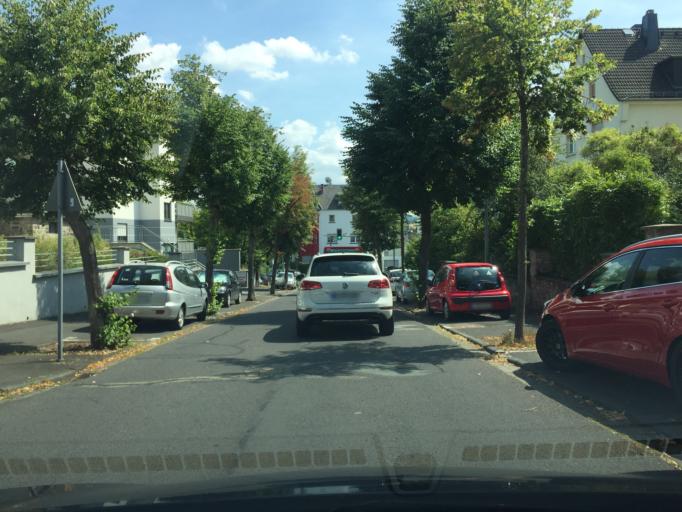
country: DE
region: Hesse
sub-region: Regierungsbezirk Giessen
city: Limburg an der Lahn
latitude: 50.3840
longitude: 8.0506
